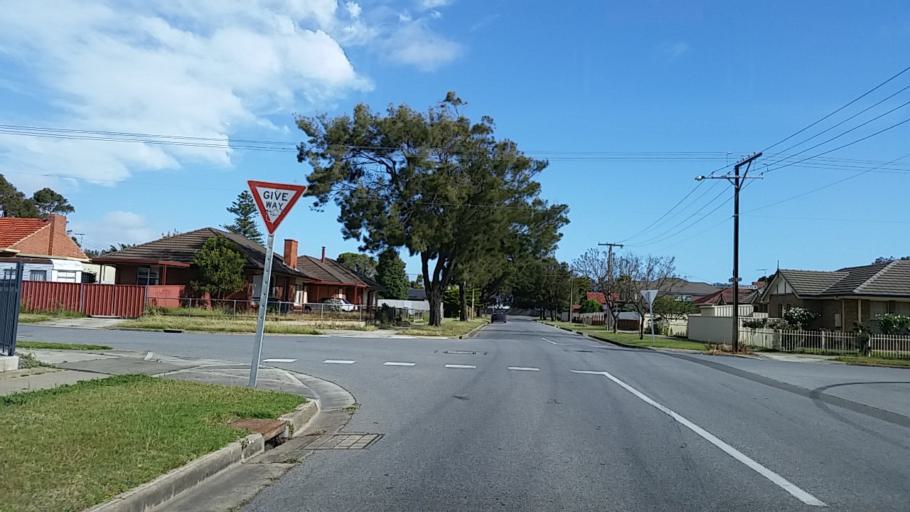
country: AU
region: South Australia
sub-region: Charles Sturt
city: Seaton
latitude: -34.8902
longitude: 138.5096
